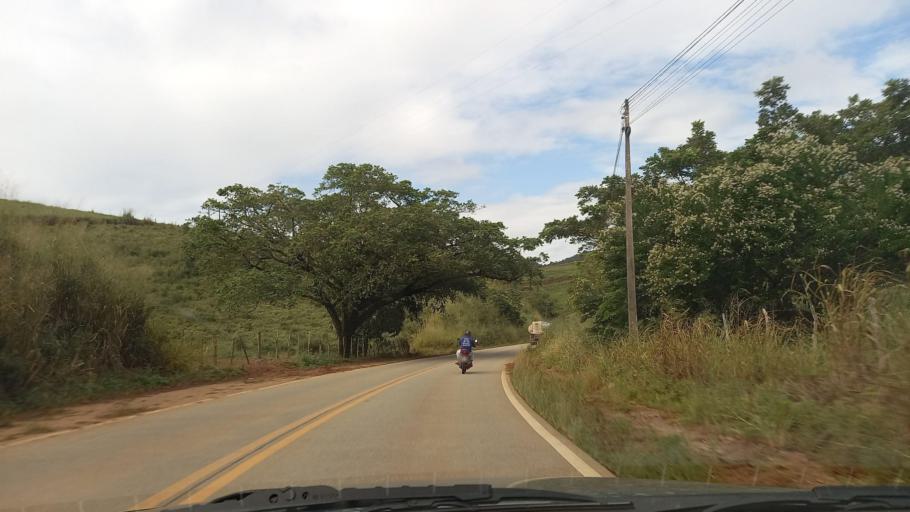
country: BR
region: Pernambuco
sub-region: Maraial
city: Maraial
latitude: -8.7464
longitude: -35.8046
